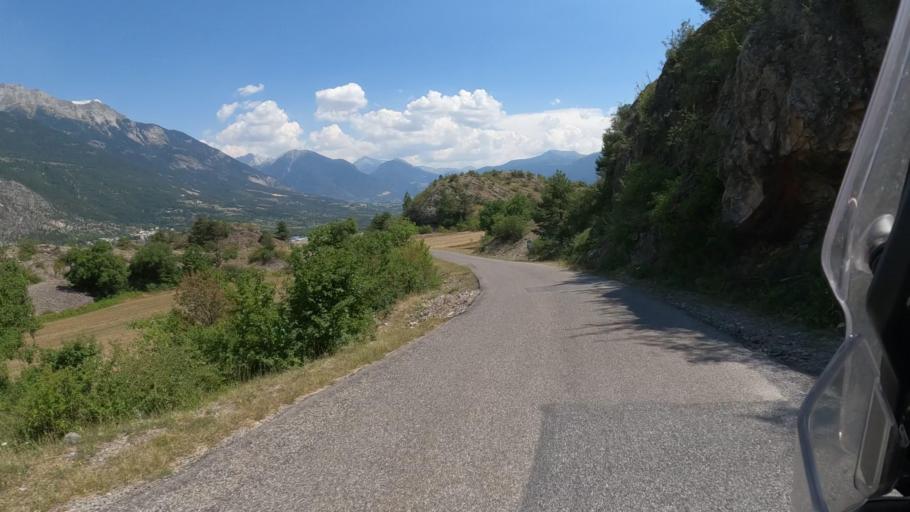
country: FR
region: Provence-Alpes-Cote d'Azur
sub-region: Departement des Hautes-Alpes
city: Guillestre
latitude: 44.7110
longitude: 6.5853
